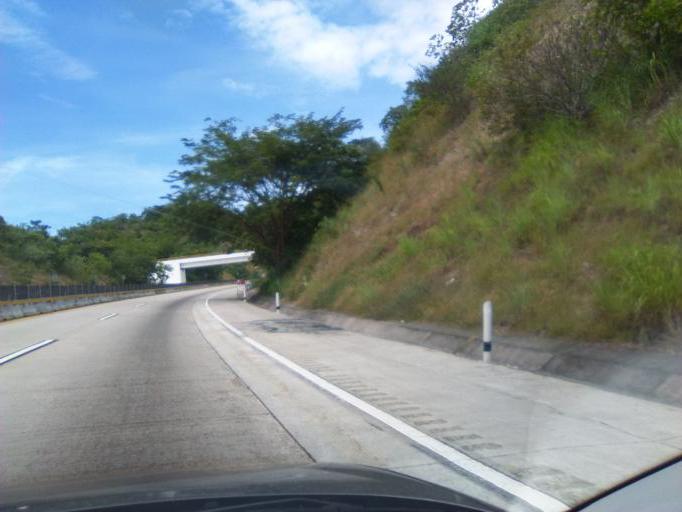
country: MX
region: Guerrero
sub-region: Chilpancingo de los Bravo
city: Julian Blanco (Dos Caminos)
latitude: 17.2038
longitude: -99.5372
